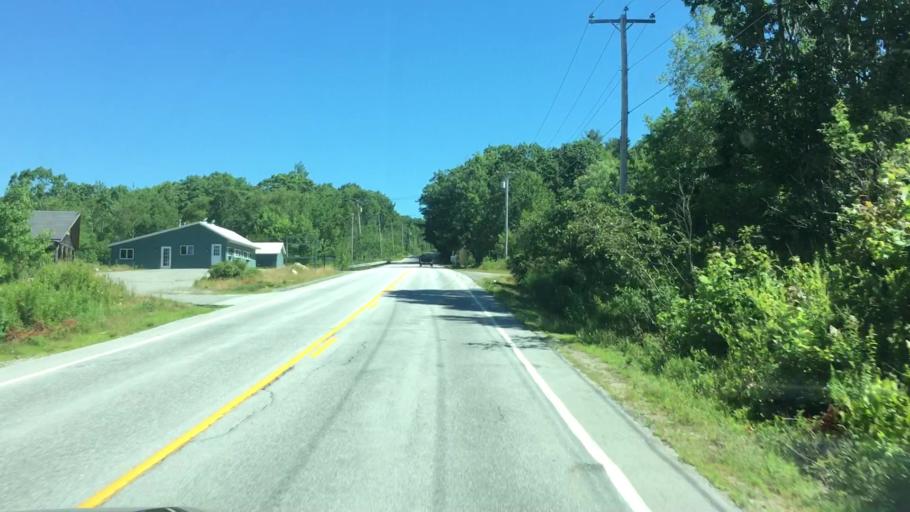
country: US
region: Maine
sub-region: Hancock County
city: Sedgwick
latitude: 44.3519
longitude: -68.6695
